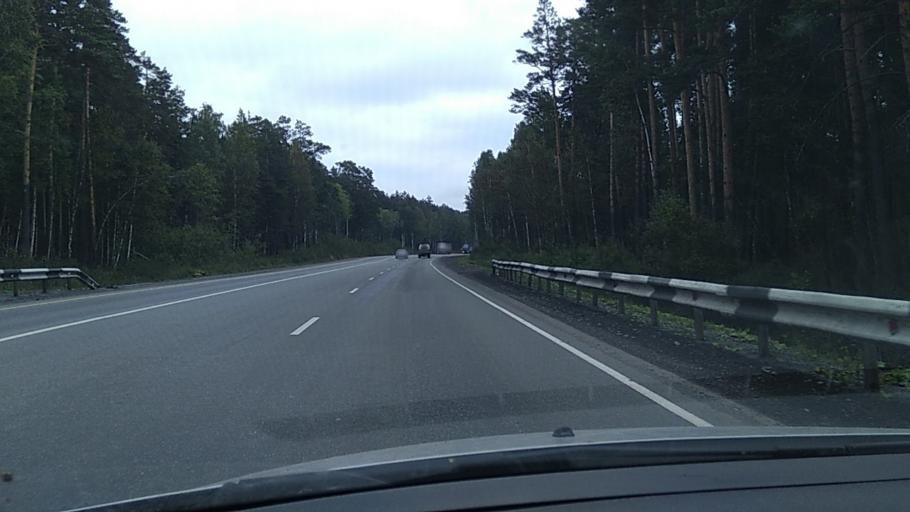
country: RU
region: Chelyabinsk
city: Zlatoust
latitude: 55.0551
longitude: 59.7066
